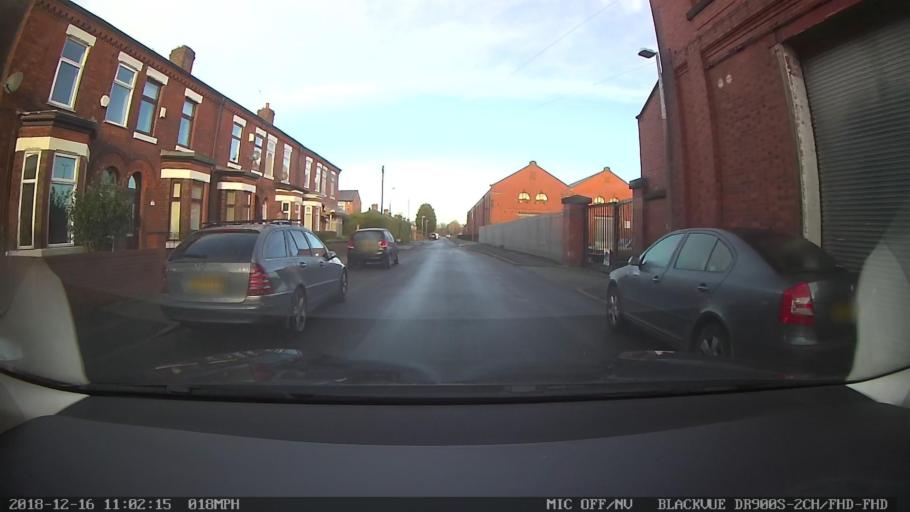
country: GB
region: England
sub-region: Manchester
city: Swinton
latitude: 53.4781
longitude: -2.3696
